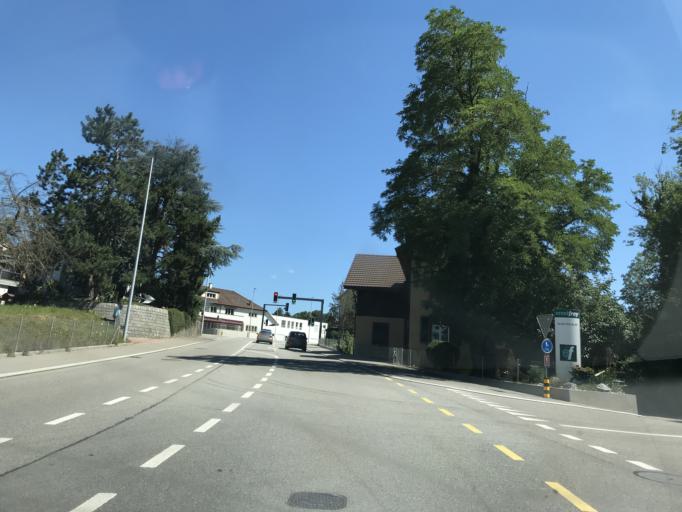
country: CH
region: Aargau
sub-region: Bezirk Rheinfelden
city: Kaiseraugst
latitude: 47.5360
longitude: 7.7207
